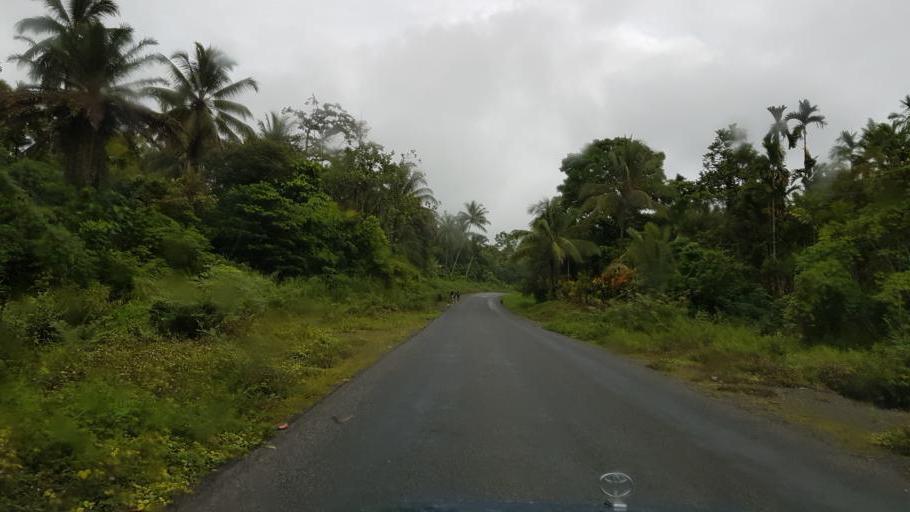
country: PG
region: Northern Province
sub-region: Sohe
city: Popondetta
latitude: -8.8278
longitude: 148.1225
